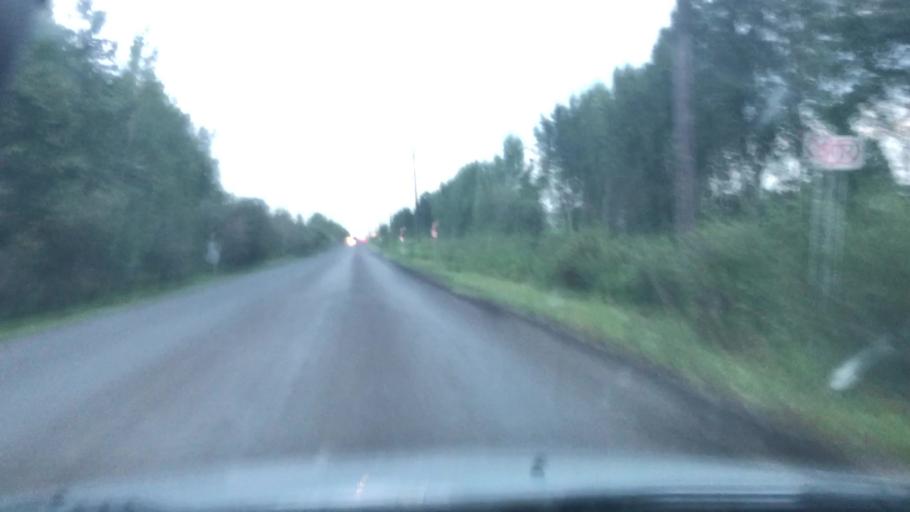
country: CA
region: Alberta
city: Devon
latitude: 53.4905
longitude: -113.6889
